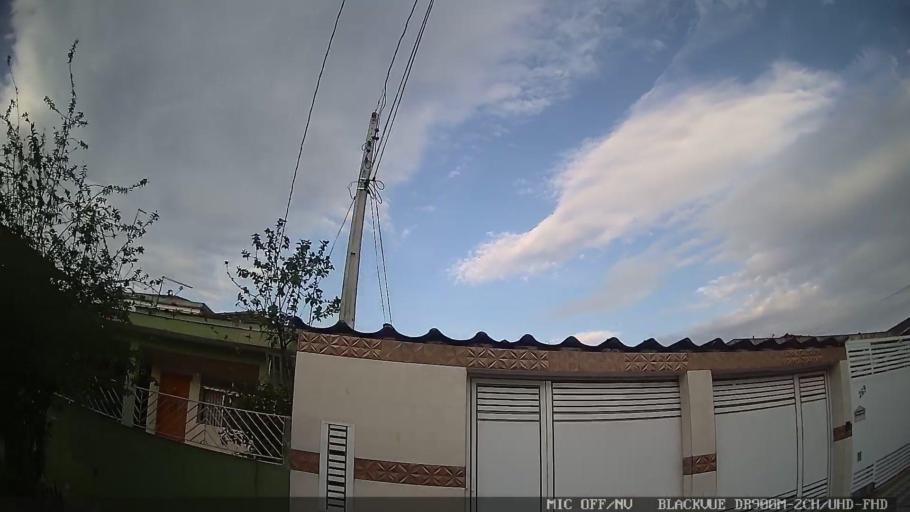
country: BR
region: Sao Paulo
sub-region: Cubatao
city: Cubatao
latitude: -23.8934
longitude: -46.4228
